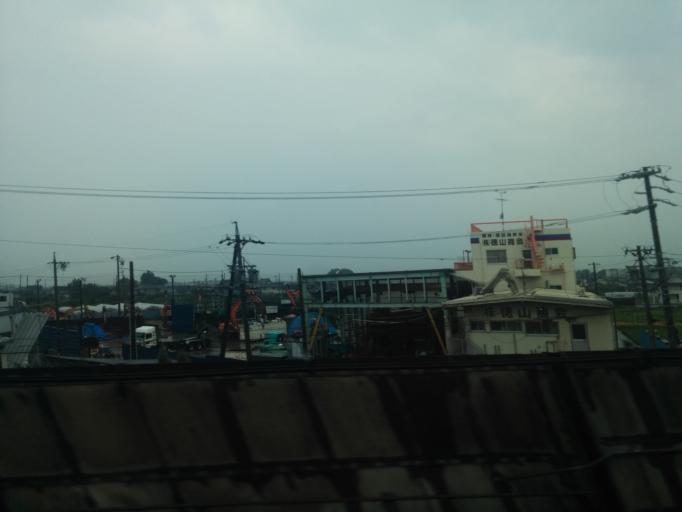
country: JP
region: Aichi
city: Inazawa
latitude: 35.2643
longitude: 136.7588
